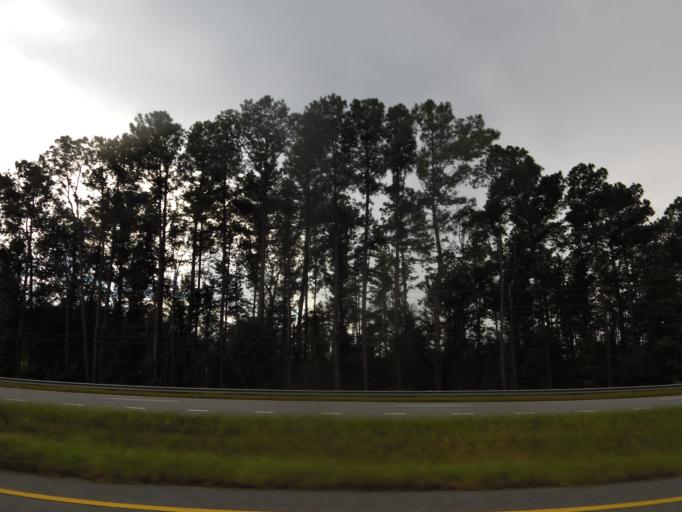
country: US
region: Georgia
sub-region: McIntosh County
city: Darien
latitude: 31.3809
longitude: -81.6339
